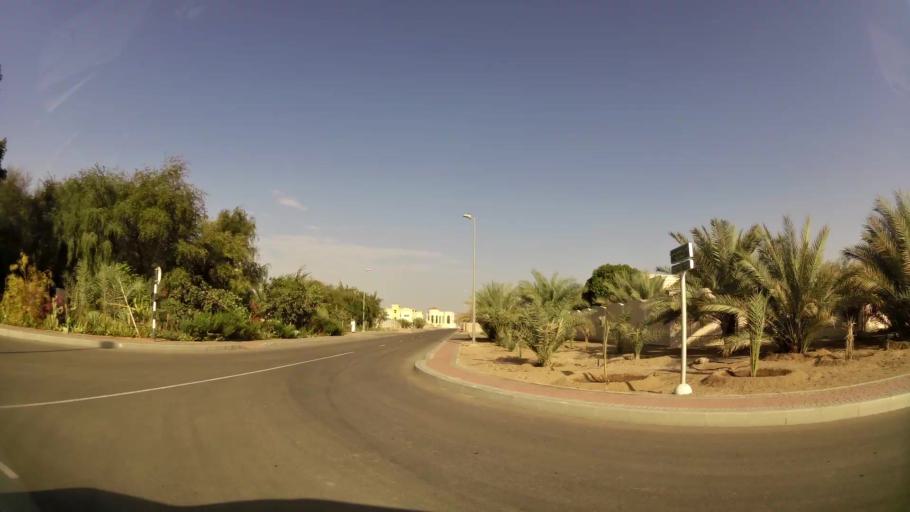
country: AE
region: Abu Dhabi
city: Al Ain
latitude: 24.0612
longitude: 55.8494
